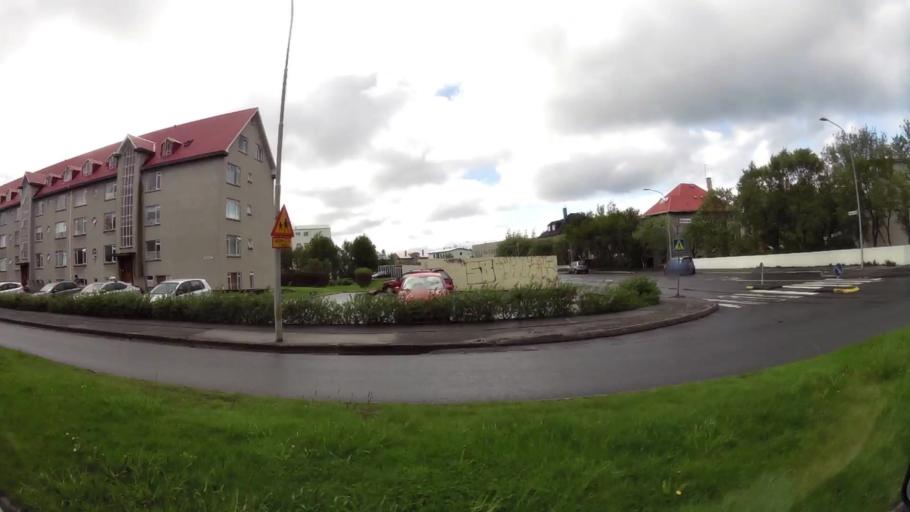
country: IS
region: Capital Region
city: Seltjarnarnes
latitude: 64.1427
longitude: -21.9607
